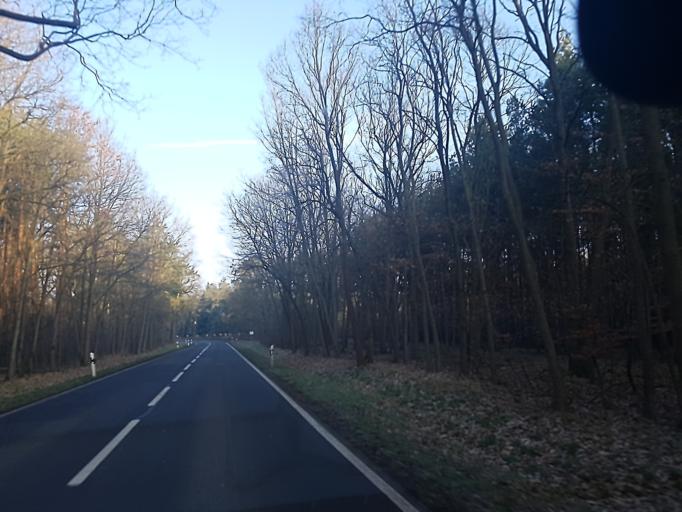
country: DE
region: Brandenburg
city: Bruck
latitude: 52.2130
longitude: 12.7501
